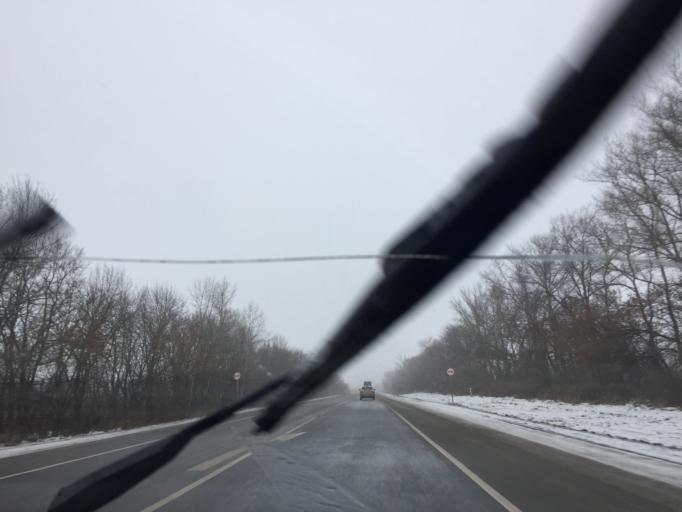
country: RU
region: Tula
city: Plavsk
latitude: 53.7996
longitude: 37.3786
